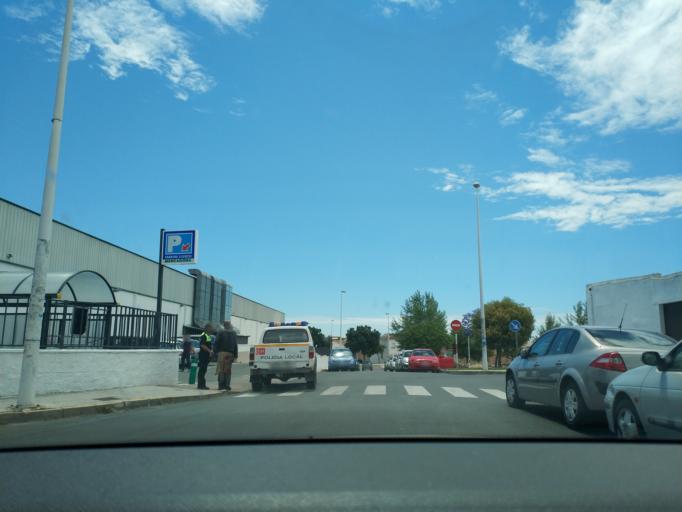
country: ES
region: Andalusia
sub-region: Provincia de Huelva
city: Cartaya
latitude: 37.2855
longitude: -7.1469
